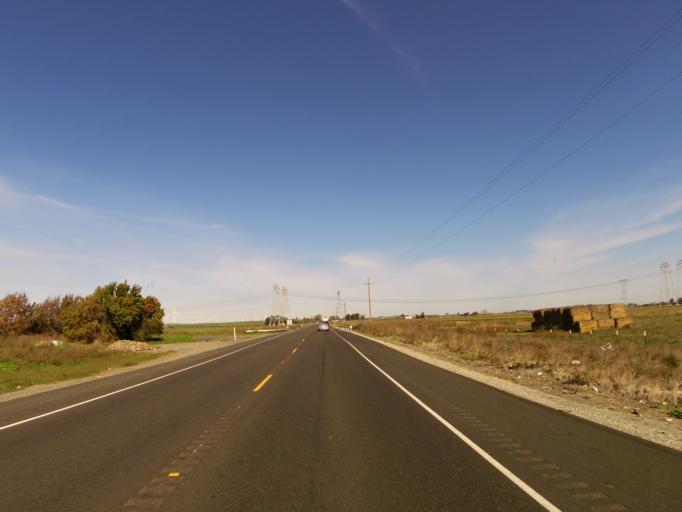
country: US
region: California
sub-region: Contra Costa County
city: Oakley
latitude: 38.0685
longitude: -121.7356
